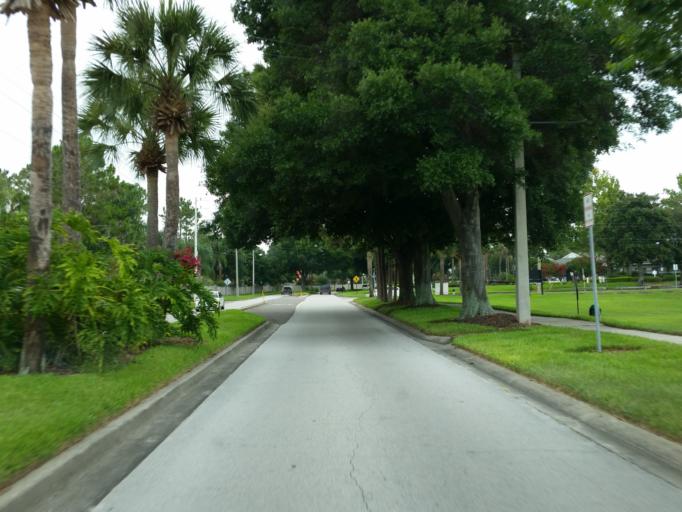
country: US
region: Florida
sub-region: Hillsborough County
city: Brandon
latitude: 27.9264
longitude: -82.2616
